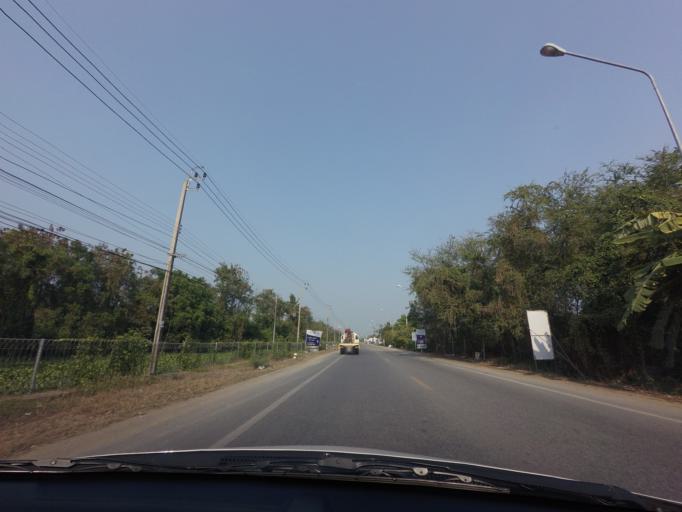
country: TH
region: Nonthaburi
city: Bang Yai
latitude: 13.8088
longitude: 100.3675
